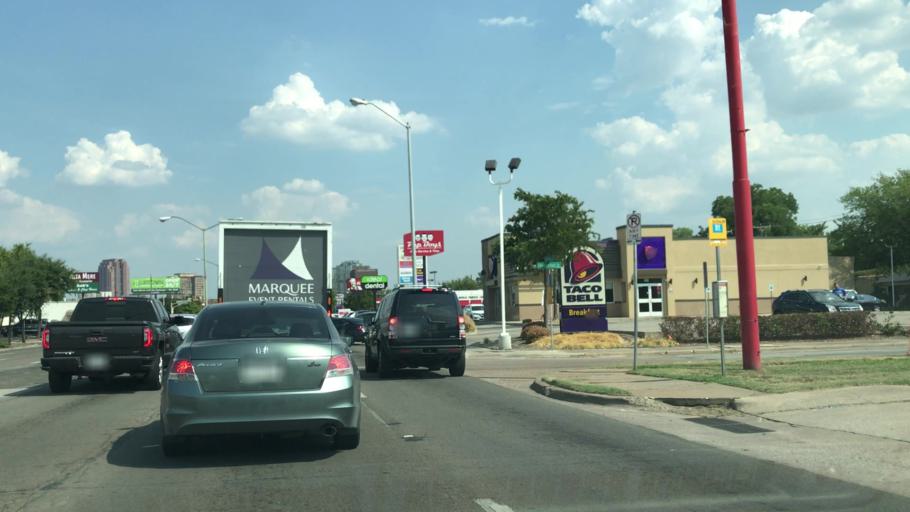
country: US
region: Texas
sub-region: Dallas County
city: Highland Park
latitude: 32.8180
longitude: -96.8128
